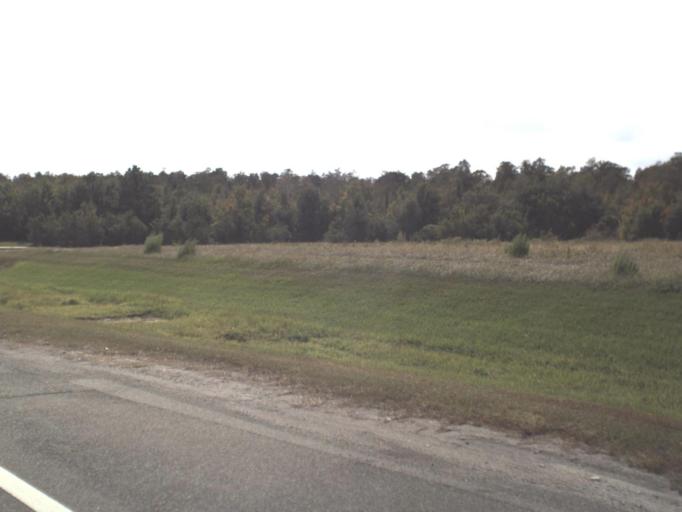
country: US
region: Florida
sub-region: Osceola County
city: Campbell
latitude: 28.2232
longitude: -81.4832
